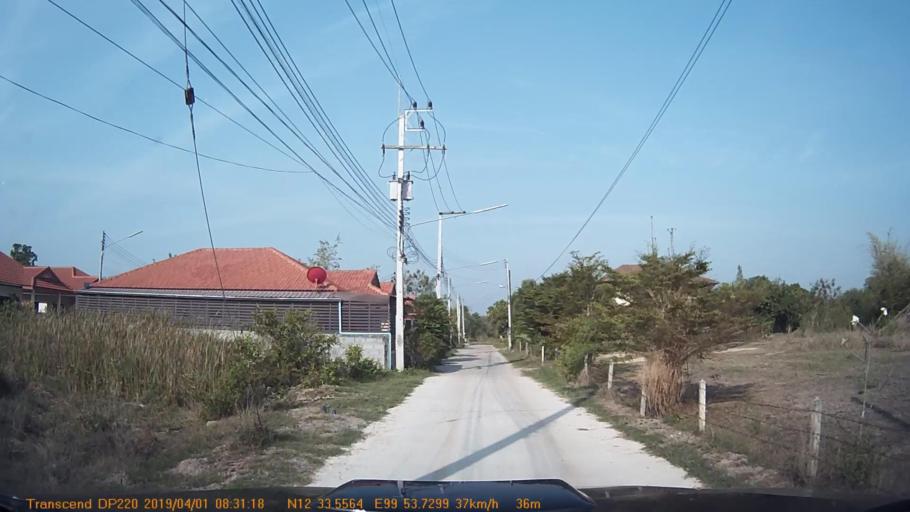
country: TH
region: Prachuap Khiri Khan
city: Hua Hin
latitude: 12.5593
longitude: 99.8955
